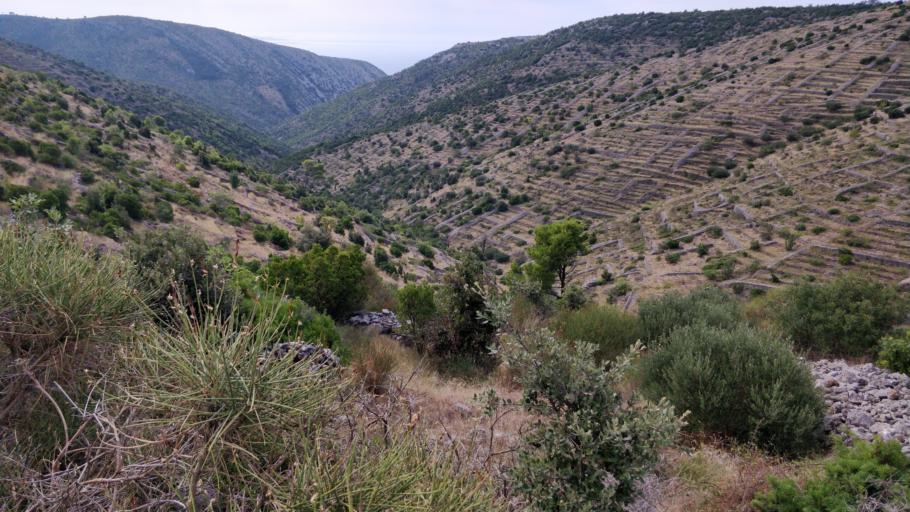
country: HR
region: Splitsko-Dalmatinska
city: Stari Grad
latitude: 43.1672
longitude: 16.5372
